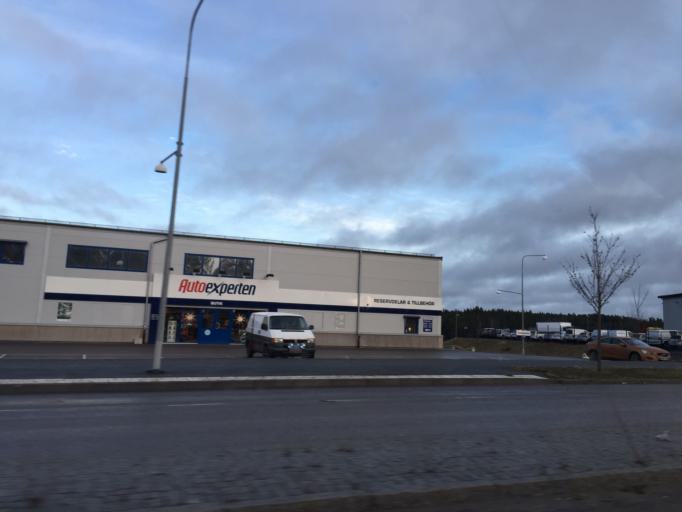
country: SE
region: Stockholm
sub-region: Sodertalje Kommun
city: Soedertaelje
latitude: 59.2070
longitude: 17.6621
